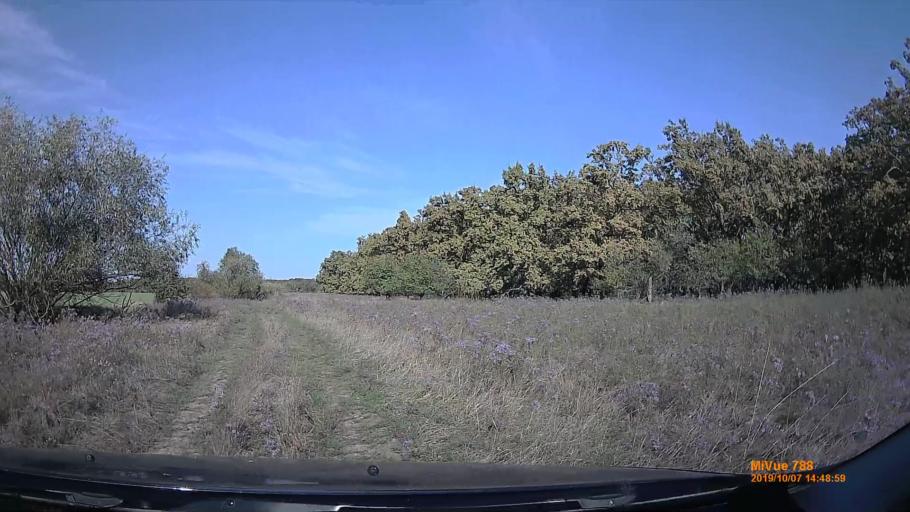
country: HU
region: Jasz-Nagykun-Szolnok
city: Kunszentmarton
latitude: 46.8588
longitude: 20.3234
